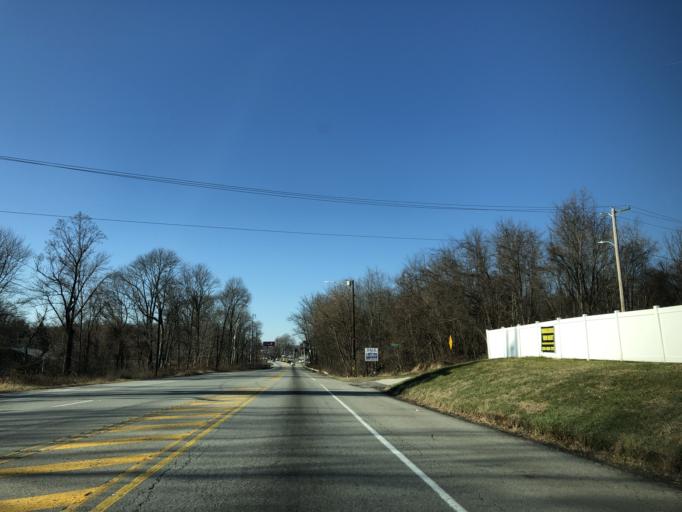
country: US
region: Pennsylvania
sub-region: Delaware County
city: Village Green-Green Ridge
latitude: 39.8475
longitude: -75.4315
